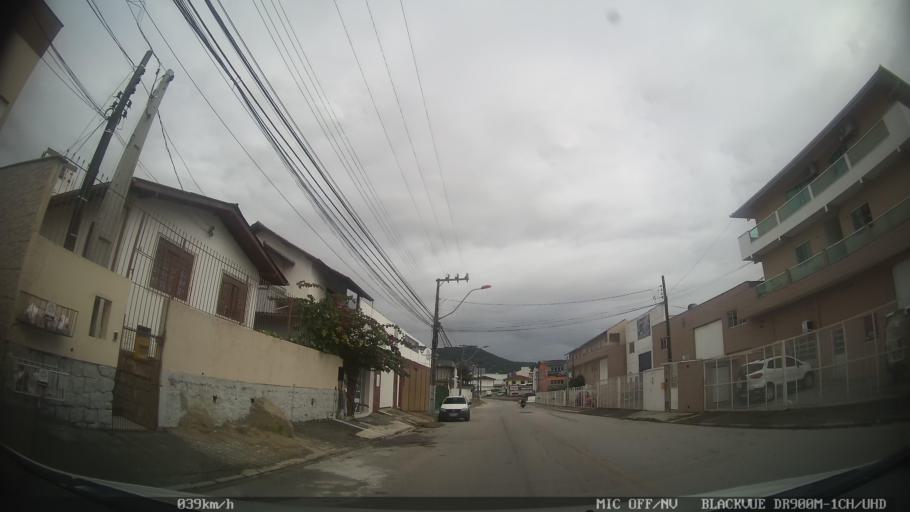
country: BR
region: Santa Catarina
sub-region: Sao Jose
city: Campinas
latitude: -27.5681
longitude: -48.6242
